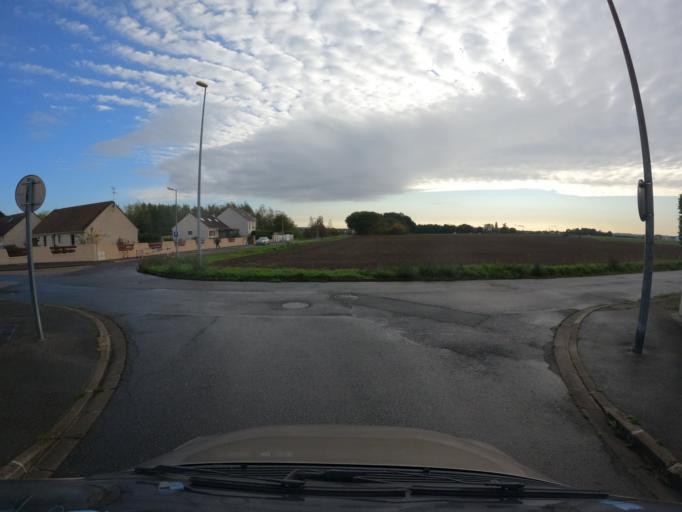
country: FR
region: Ile-de-France
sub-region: Departement de Seine-et-Marne
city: Courtry
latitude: 48.8999
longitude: 2.6080
